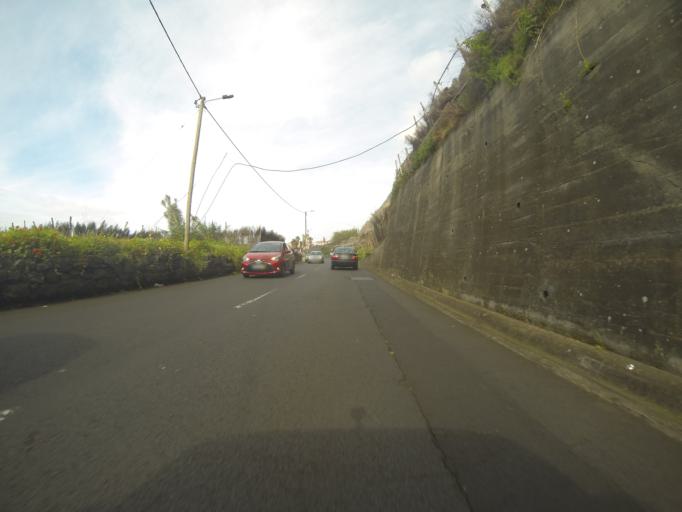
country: PT
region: Madeira
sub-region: Sao Vicente
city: Sao Vicente
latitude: 32.8113
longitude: -17.0390
